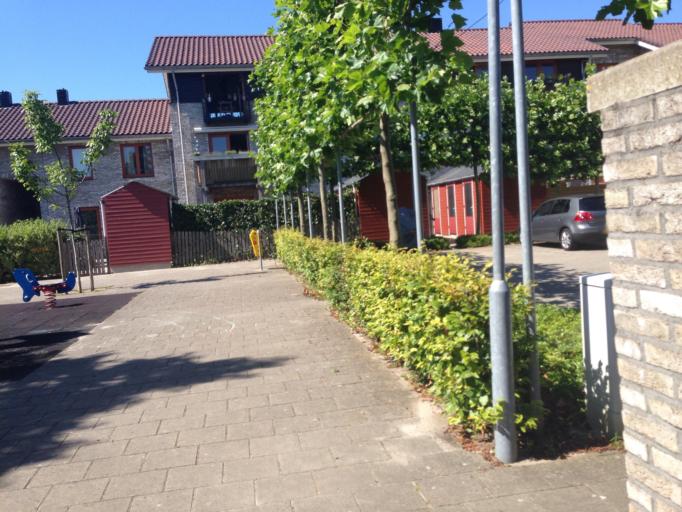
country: NL
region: Flevoland
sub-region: Gemeente Almere
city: Almere Stad
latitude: 52.4064
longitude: 5.3154
